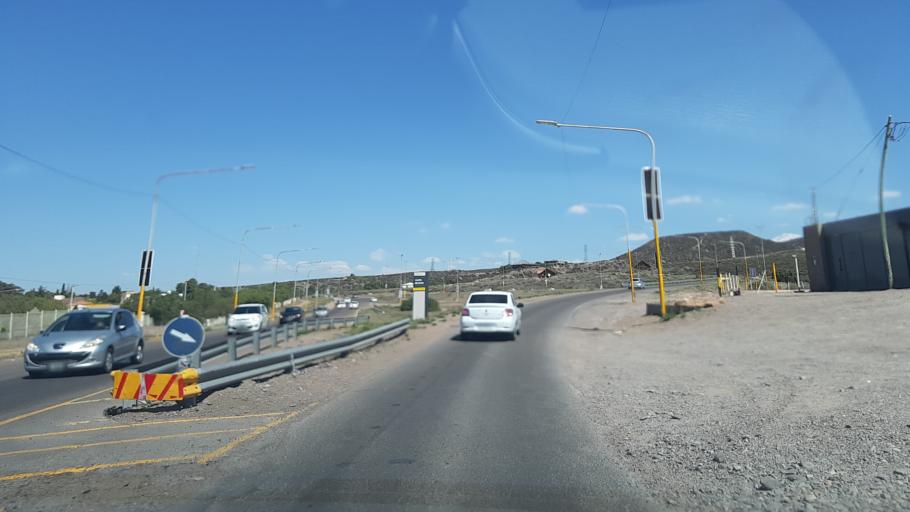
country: AR
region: Mendoza
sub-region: Departamento de Godoy Cruz
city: Godoy Cruz
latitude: -32.9694
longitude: -68.8780
